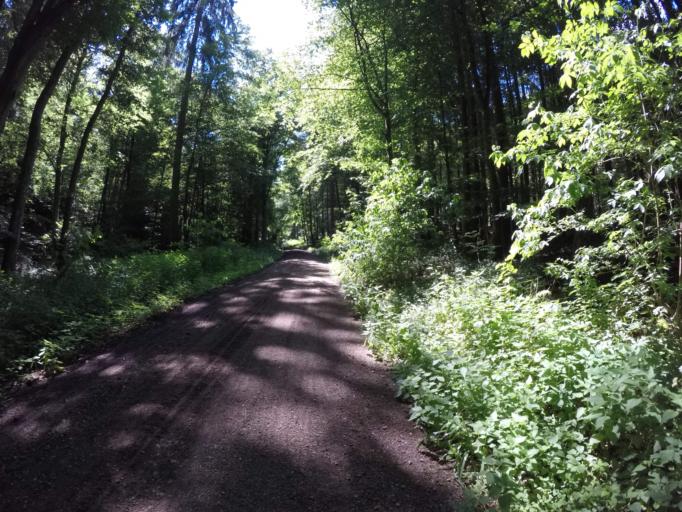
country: DE
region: Bavaria
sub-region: Lower Bavaria
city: Essing
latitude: 48.9240
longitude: 11.7890
